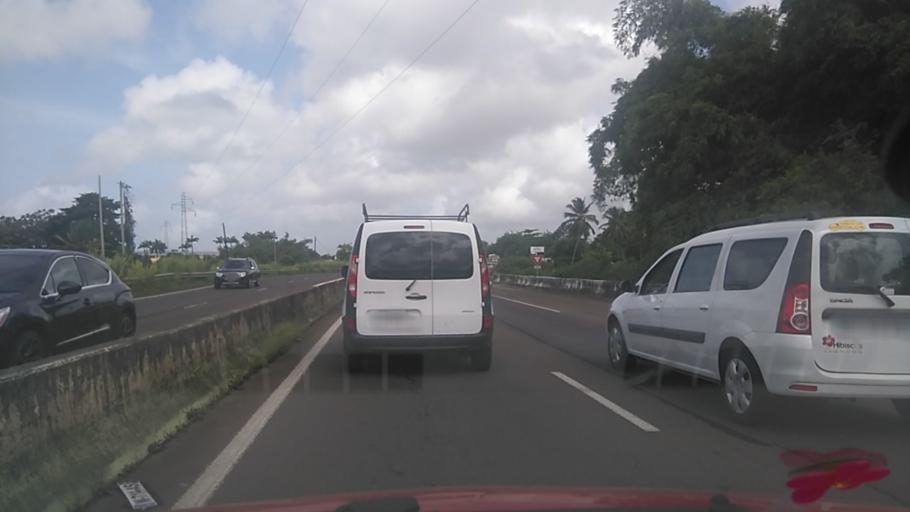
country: MQ
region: Martinique
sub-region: Martinique
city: Le Lamentin
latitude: 14.6250
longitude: -60.9840
